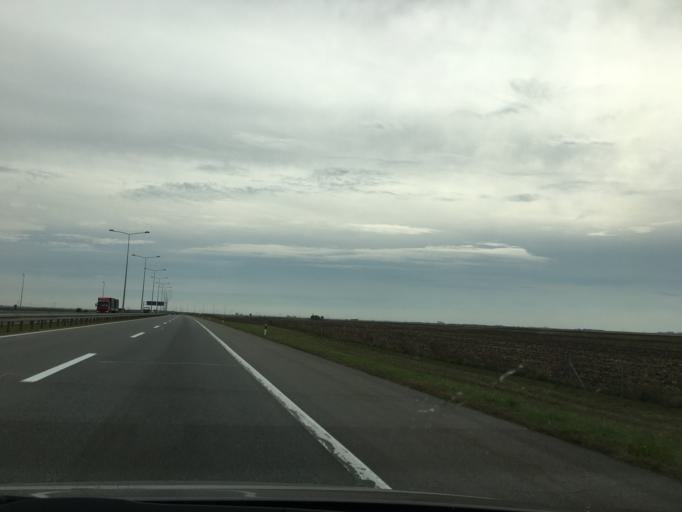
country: RS
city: Krcedin
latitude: 45.1007
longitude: 20.1129
